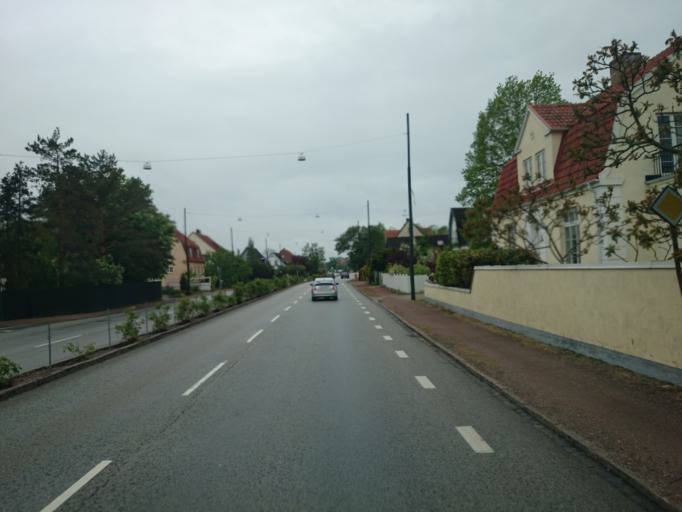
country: SE
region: Skane
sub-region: Malmo
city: Bunkeflostrand
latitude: 55.5846
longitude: 12.9490
